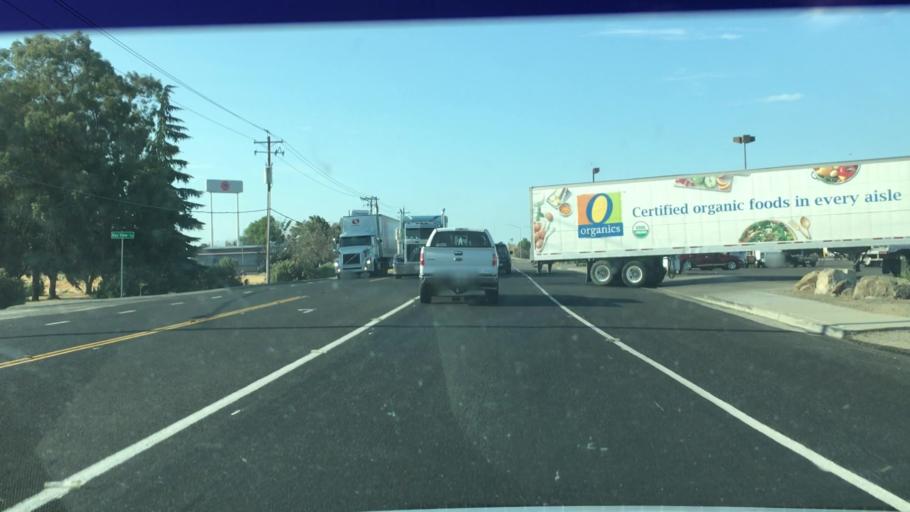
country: US
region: California
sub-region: Merced County
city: Gustine
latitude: 37.1015
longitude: -121.0159
